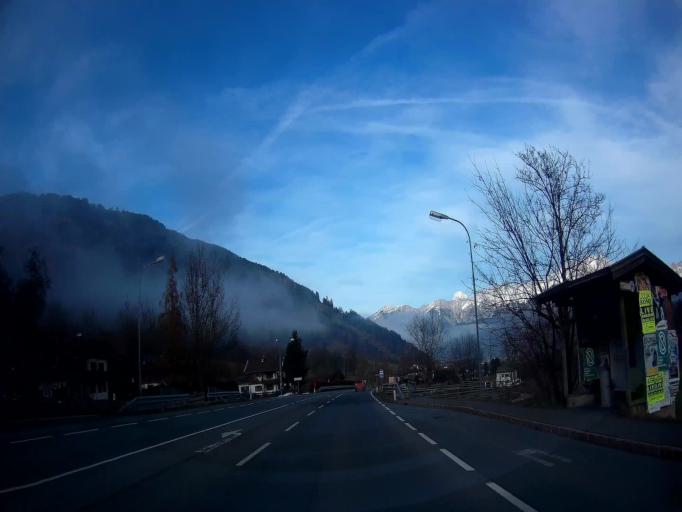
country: AT
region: Salzburg
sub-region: Politischer Bezirk Zell am See
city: Maishofen
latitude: 47.3961
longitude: 12.8005
